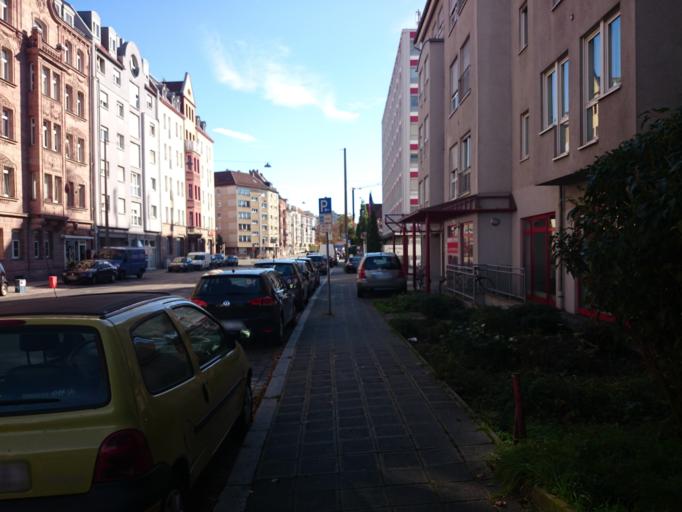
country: DE
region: Bavaria
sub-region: Regierungsbezirk Mittelfranken
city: Nuernberg
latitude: 49.4454
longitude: 11.0962
